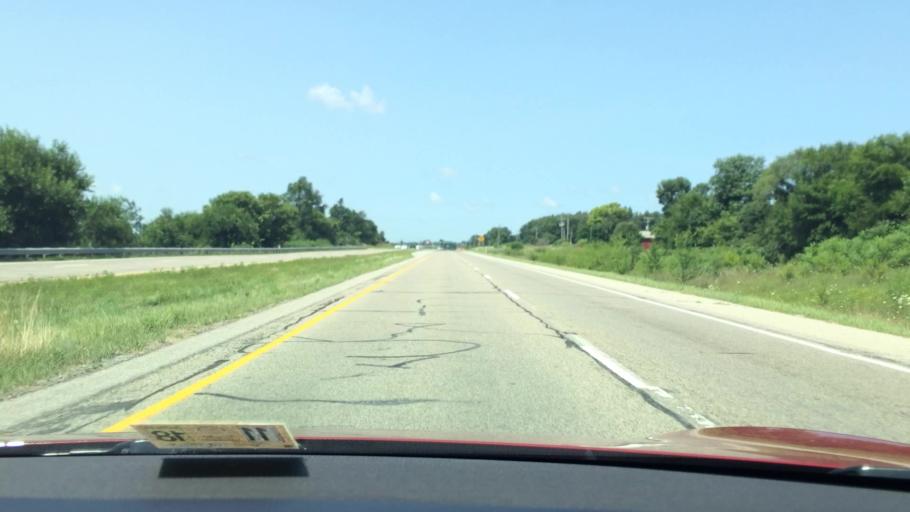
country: US
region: Indiana
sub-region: LaPorte County
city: Hudson Lake
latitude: 41.6729
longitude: -86.5799
